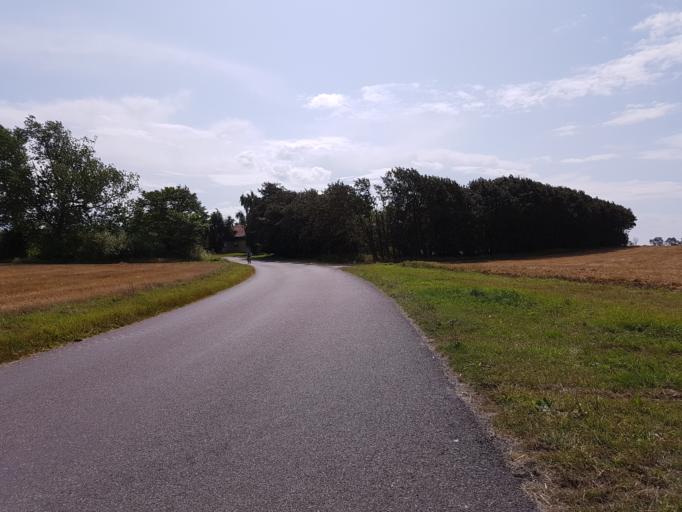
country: DK
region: Zealand
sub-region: Guldborgsund Kommune
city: Nykobing Falster
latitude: 54.5989
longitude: 11.9420
